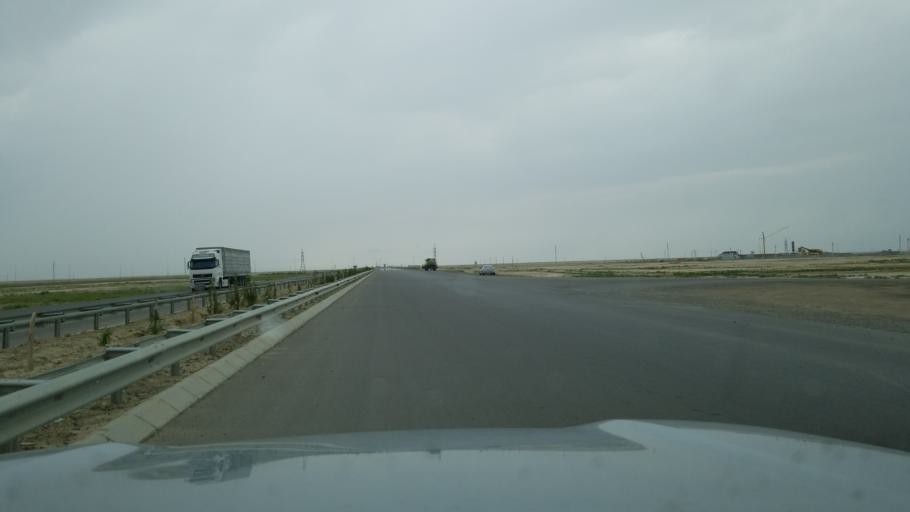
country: TM
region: Balkan
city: Serdar
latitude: 39.0053
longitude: 56.2513
